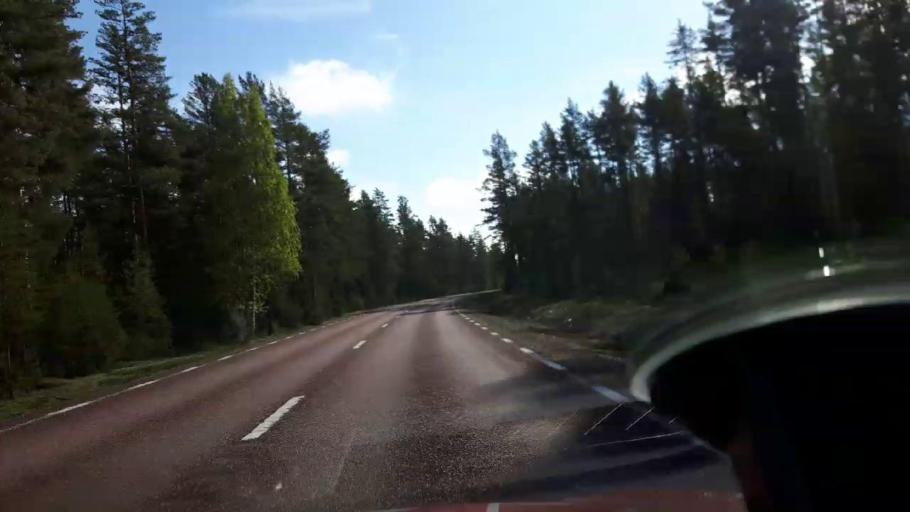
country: SE
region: Gaevleborg
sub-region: Ljusdals Kommun
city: Farila
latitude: 61.9200
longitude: 15.6111
